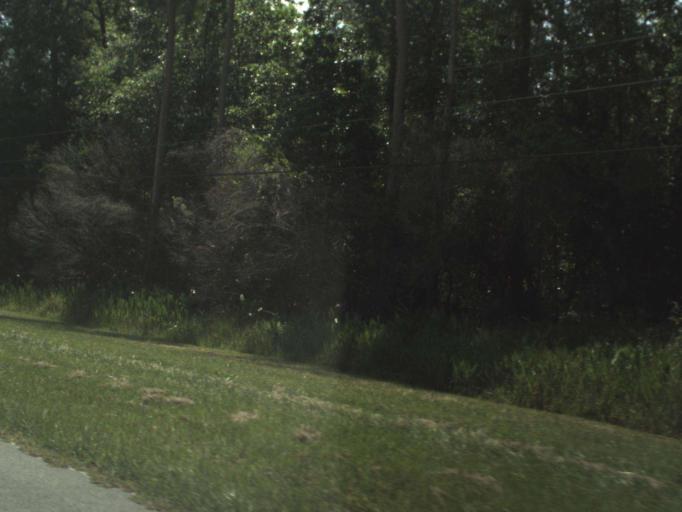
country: US
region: Florida
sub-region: Volusia County
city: Samsula-Spruce Creek
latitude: 29.1249
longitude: -81.1677
